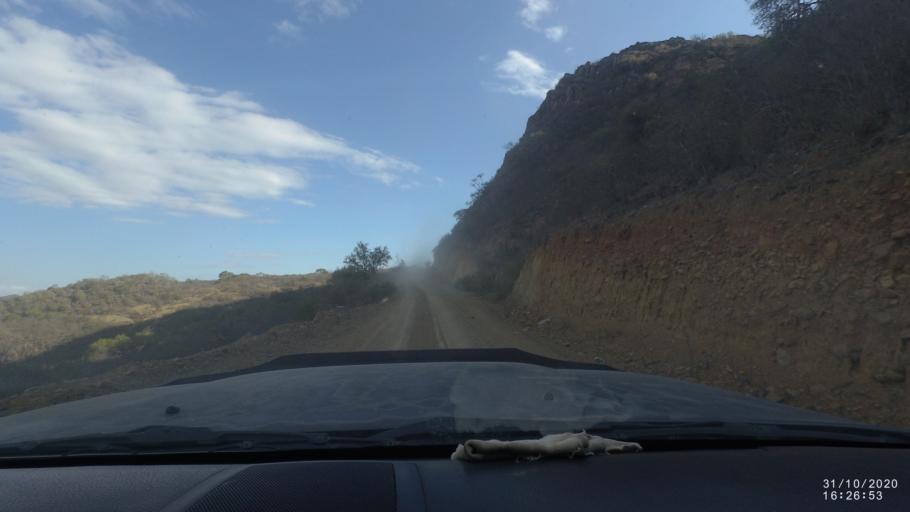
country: BO
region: Chuquisaca
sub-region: Provincia Zudanez
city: Mojocoya
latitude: -18.4021
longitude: -64.5859
